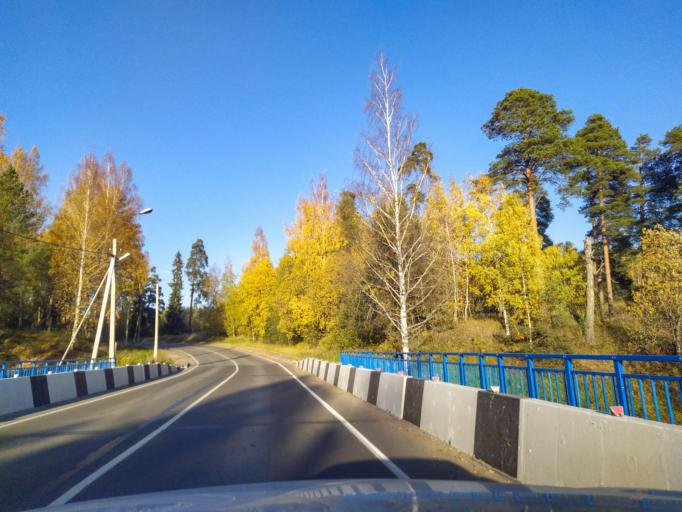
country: RU
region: Leningrad
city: Siverskiy
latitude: 59.3467
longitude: 30.0580
